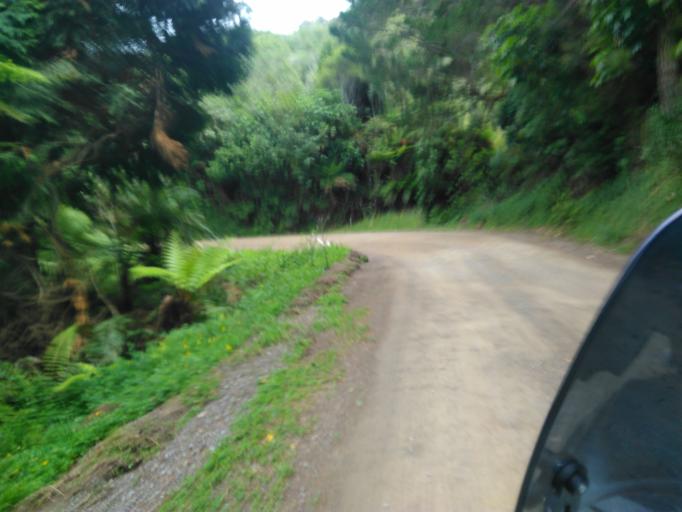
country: NZ
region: Bay of Plenty
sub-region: Opotiki District
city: Opotiki
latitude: -38.1068
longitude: 177.5018
